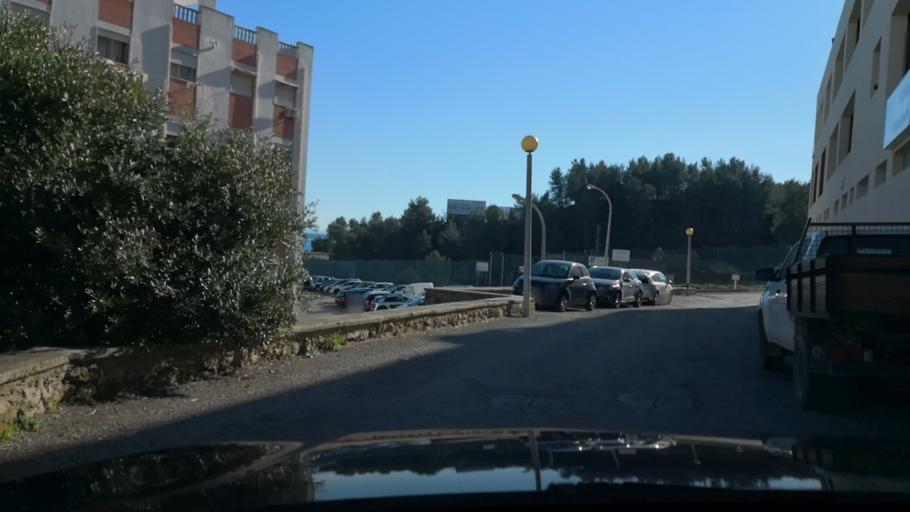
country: PT
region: Setubal
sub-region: Setubal
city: Setubal
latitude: 38.5244
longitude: -8.9062
